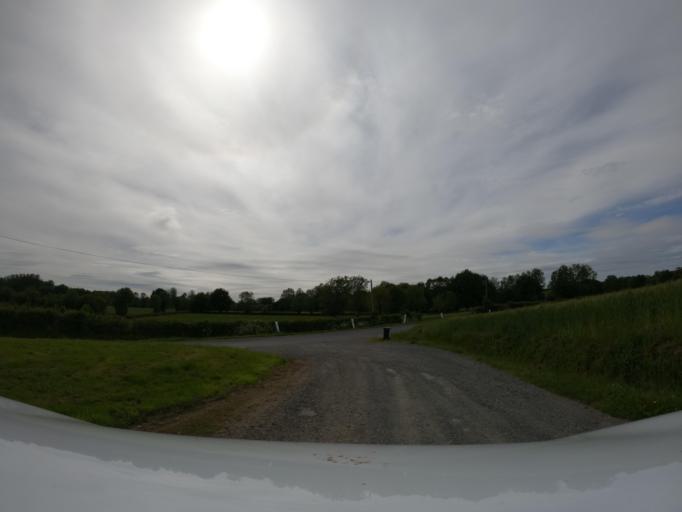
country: FR
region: Pays de la Loire
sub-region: Departement de la Vendee
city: Foussais-Payre
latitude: 46.5138
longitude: -0.6502
